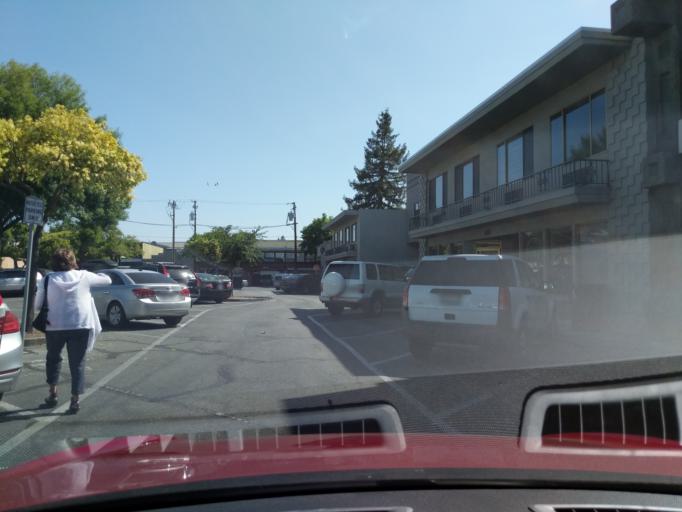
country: US
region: California
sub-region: San Mateo County
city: Menlo Park
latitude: 37.4519
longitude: -122.1832
